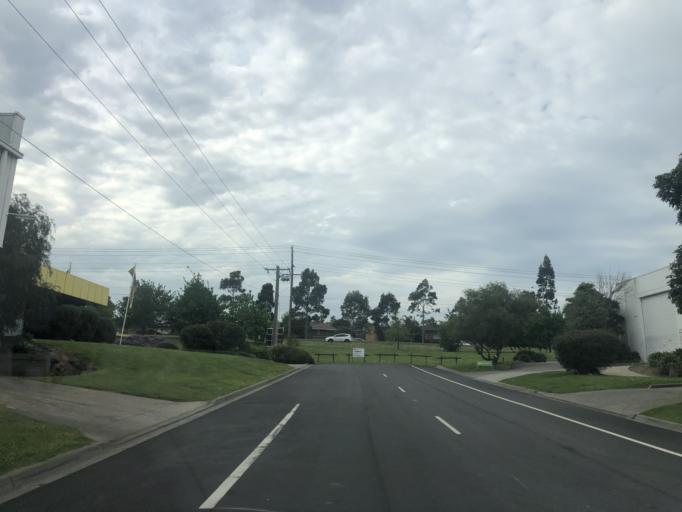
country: AU
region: Victoria
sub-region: Casey
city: Eumemmerring
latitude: -38.0051
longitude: 145.2566
